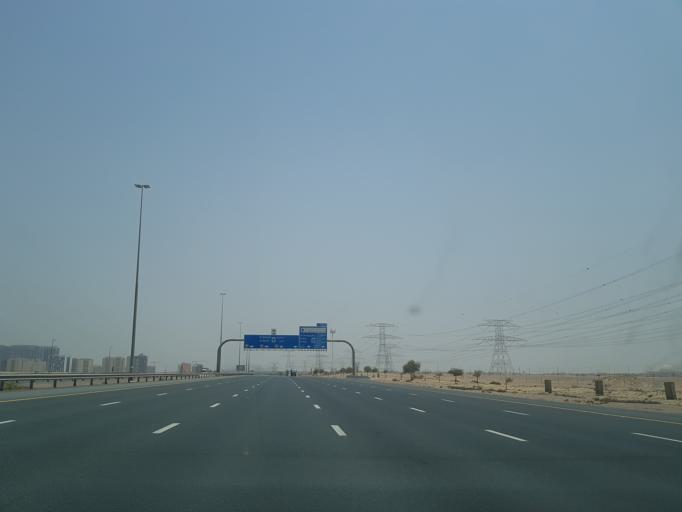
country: AE
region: Dubai
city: Dubai
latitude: 25.0757
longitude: 55.3747
